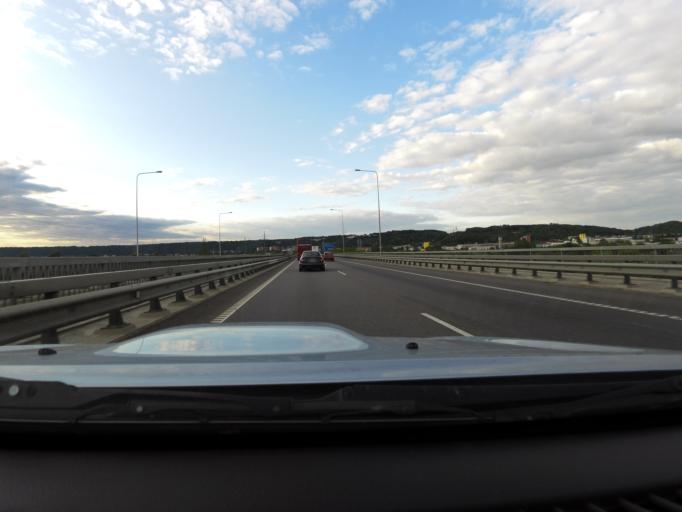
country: LT
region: Kauno apskritis
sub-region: Kauno rajonas
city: Akademija (Kaunas)
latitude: 54.9072
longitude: 23.8341
